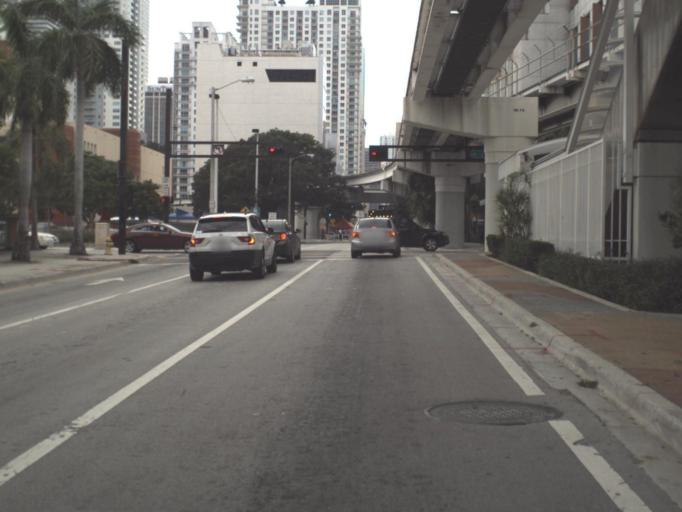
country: US
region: Florida
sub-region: Miami-Dade County
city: Miami
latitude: 25.7805
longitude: -80.1905
